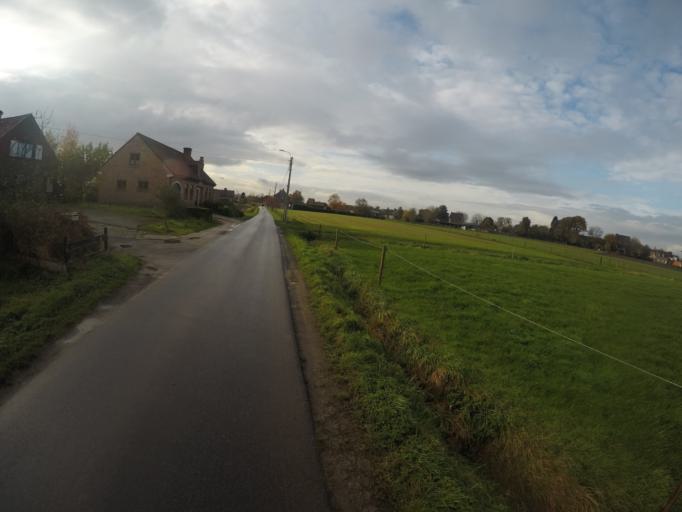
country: BE
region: Flanders
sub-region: Provincie Antwerpen
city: Zwijndrecht
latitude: 51.2076
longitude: 4.3019
